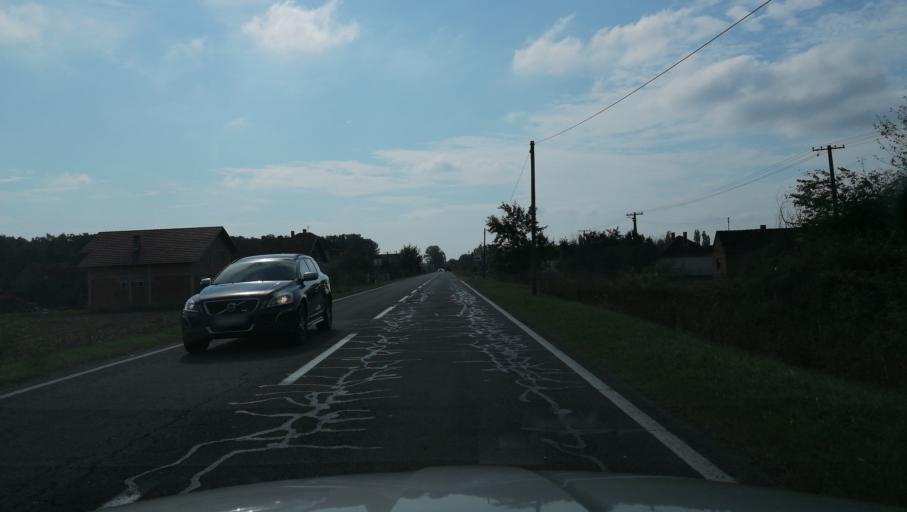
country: RS
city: Bosut
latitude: 44.9493
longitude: 19.3710
